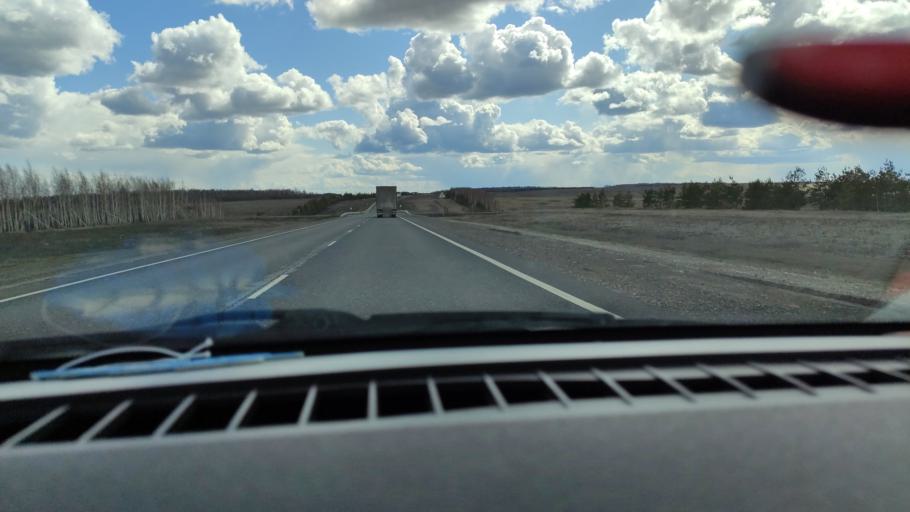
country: RU
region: Samara
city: Syzran'
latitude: 52.8847
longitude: 48.2934
